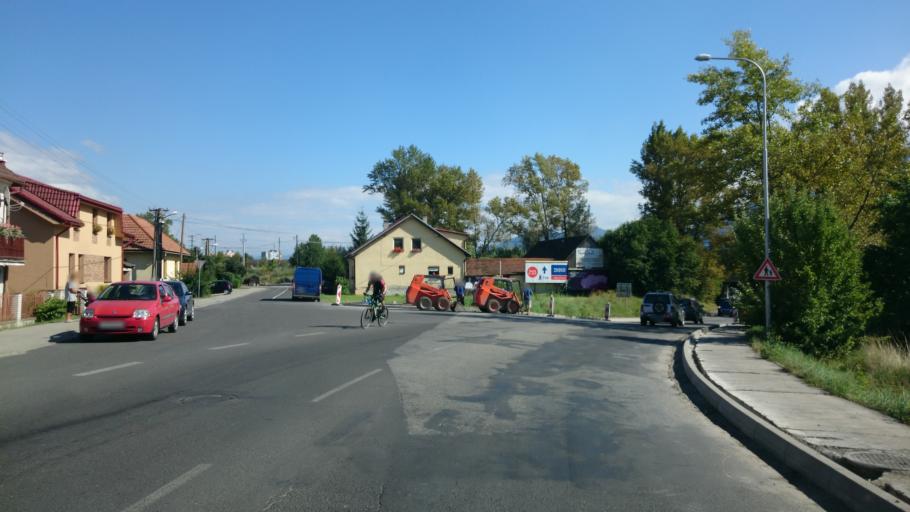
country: SK
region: Zilinsky
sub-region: Okres Liptovsky Mikulas
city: Liptovsky Mikulas
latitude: 49.0948
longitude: 19.5896
